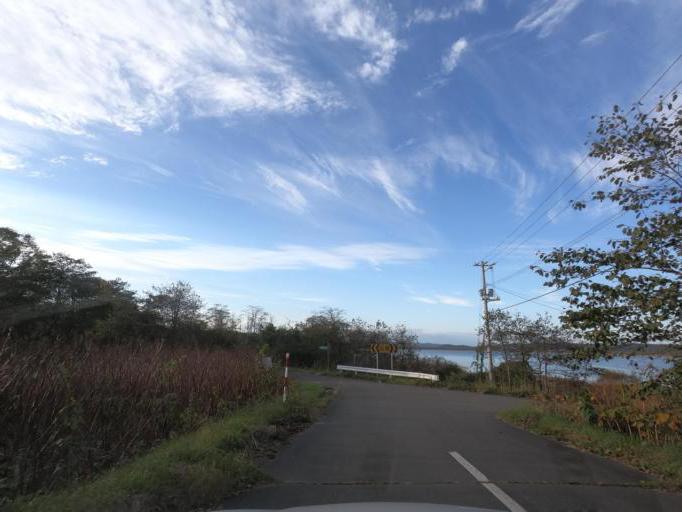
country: JP
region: Hokkaido
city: Obihiro
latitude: 42.5458
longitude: 143.4933
